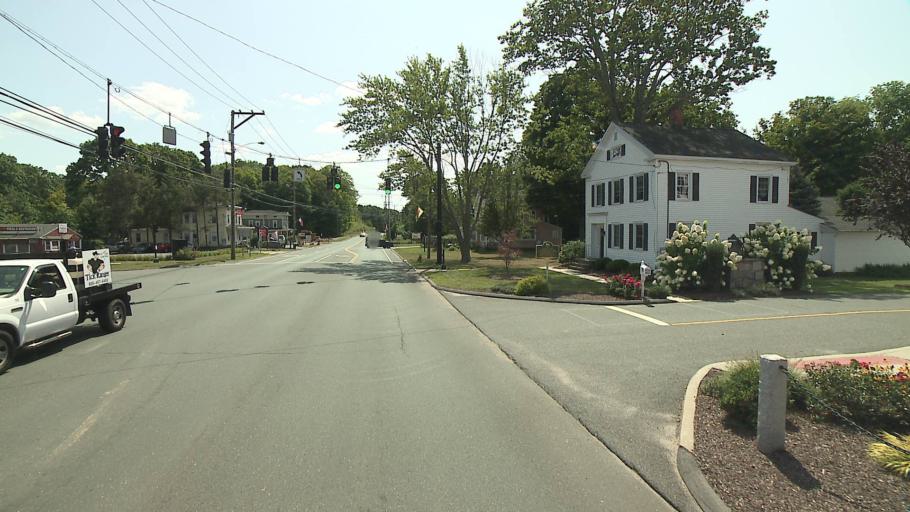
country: US
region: Connecticut
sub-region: Fairfield County
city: Newtown
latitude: 41.3216
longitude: -73.2643
